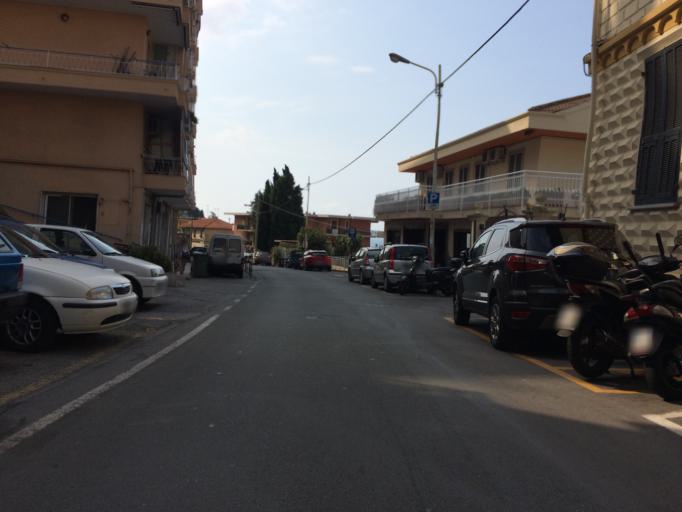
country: IT
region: Liguria
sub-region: Provincia di Imperia
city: San Remo
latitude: 43.8264
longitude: 7.7732
